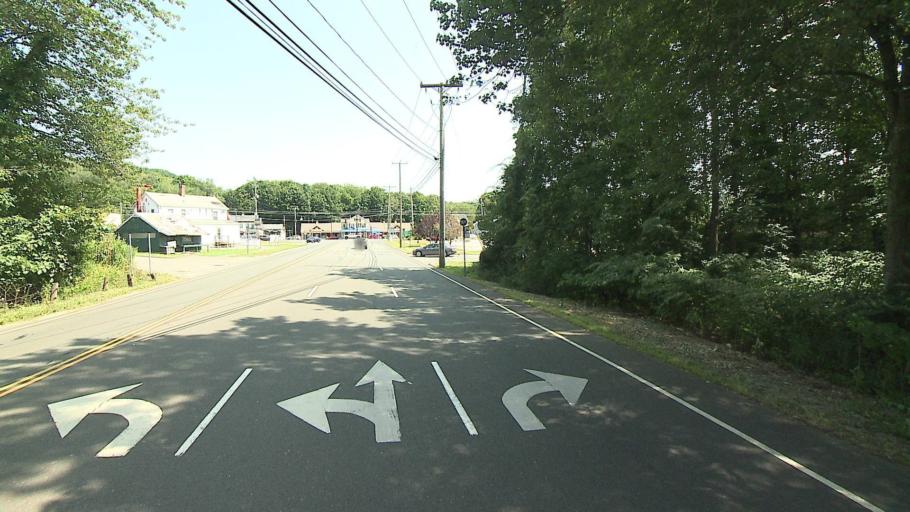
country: US
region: Connecticut
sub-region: Fairfield County
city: Newtown
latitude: 41.3221
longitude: -73.2667
